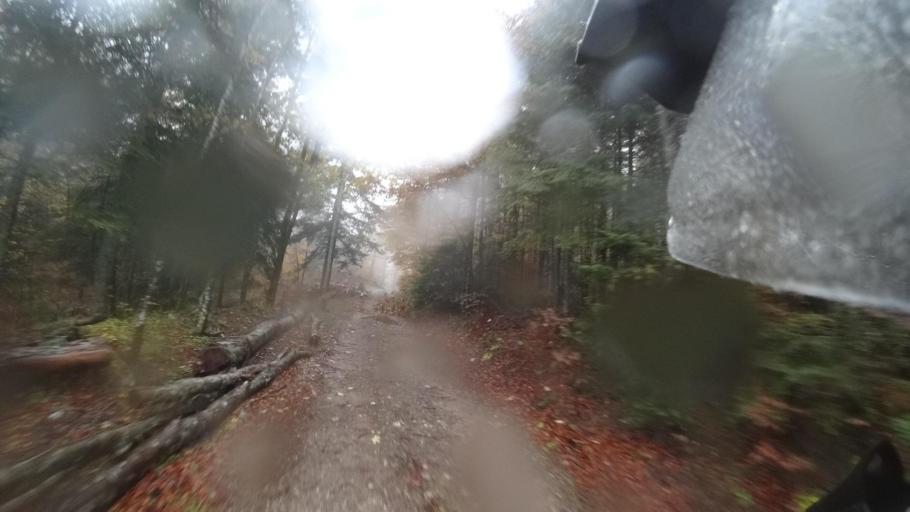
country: HR
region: Primorsko-Goranska
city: Vrbovsko
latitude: 45.2925
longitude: 14.9416
